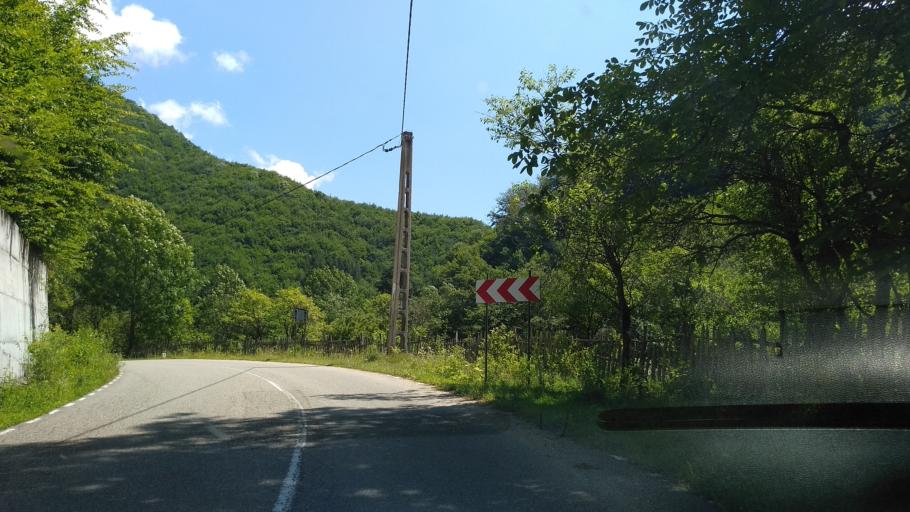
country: RO
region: Hunedoara
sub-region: Comuna Orastioara de Sus
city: Orastioara de Sus
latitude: 45.6548
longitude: 23.1849
